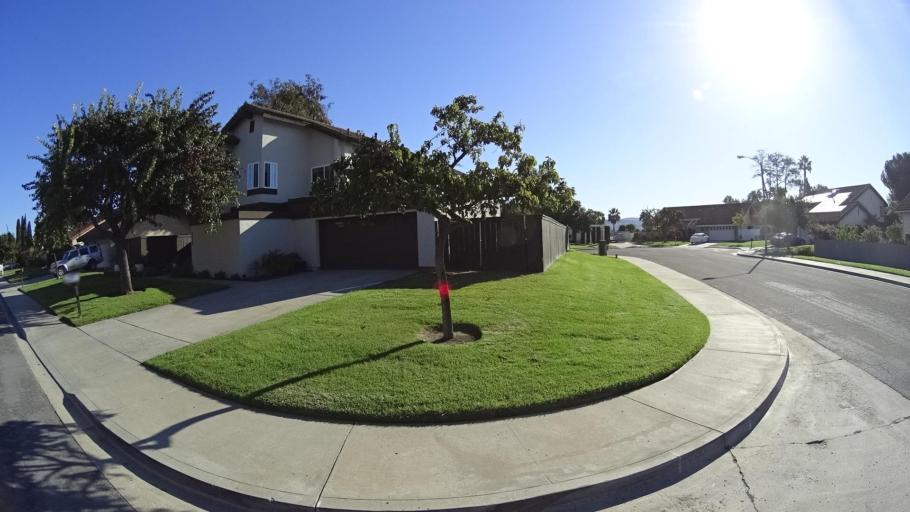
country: US
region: California
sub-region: San Diego County
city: Bonita
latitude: 32.6756
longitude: -117.0296
